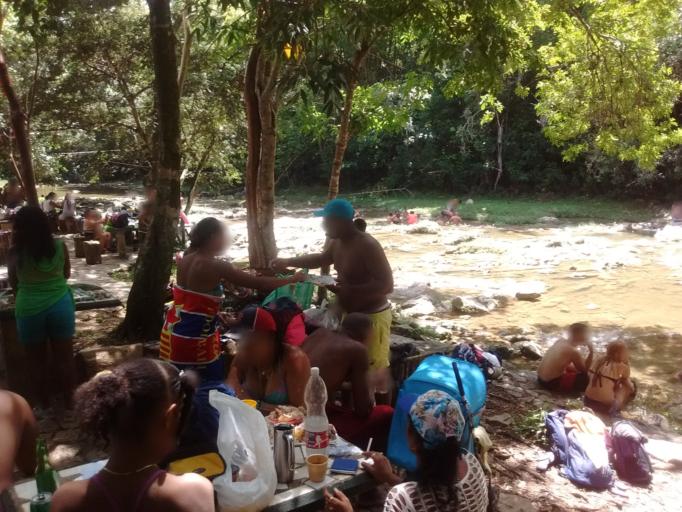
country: CU
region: Artemisa
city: Soroa
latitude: 22.8233
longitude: -82.9267
